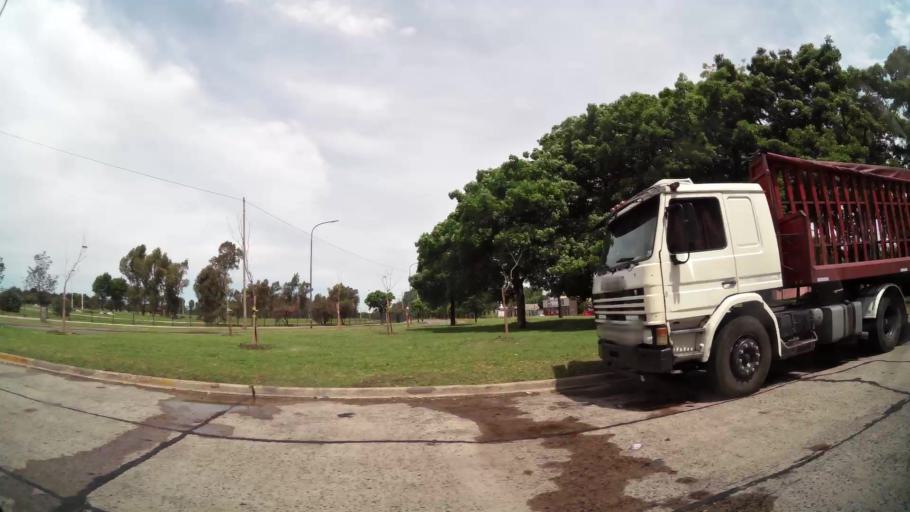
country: AR
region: Buenos Aires F.D.
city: Villa Lugano
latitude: -34.6649
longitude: -58.4689
